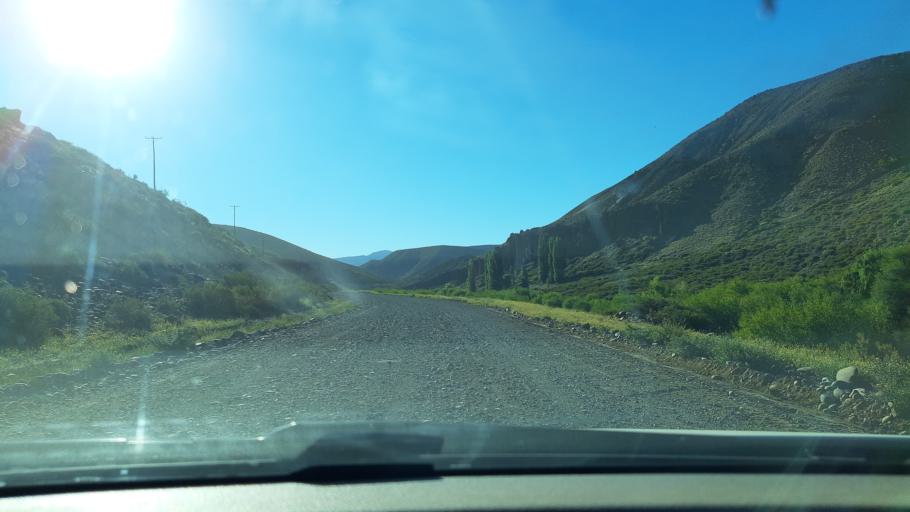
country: AR
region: Neuquen
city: Las Ovejas
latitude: -36.8105
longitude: -70.7088
